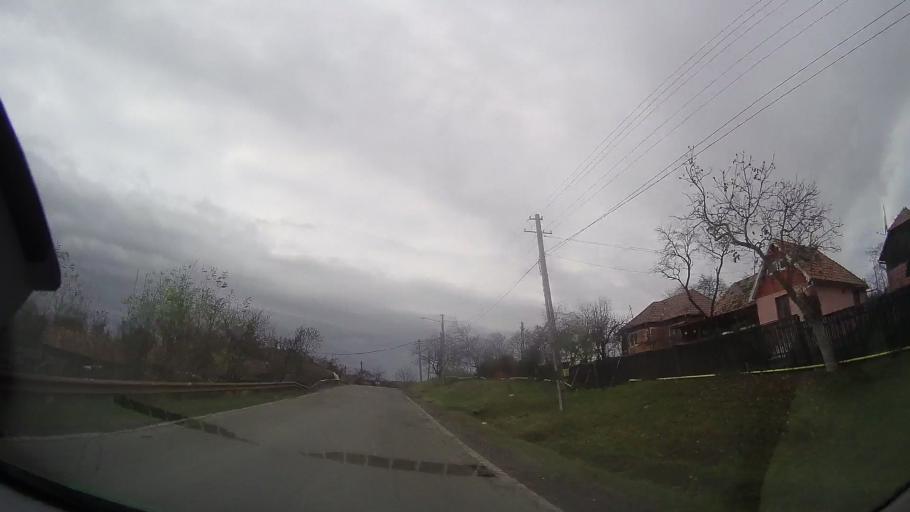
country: RO
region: Bistrita-Nasaud
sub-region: Comuna Silvasu de Campie
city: Silvasu de Campie
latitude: 46.7772
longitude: 24.3140
